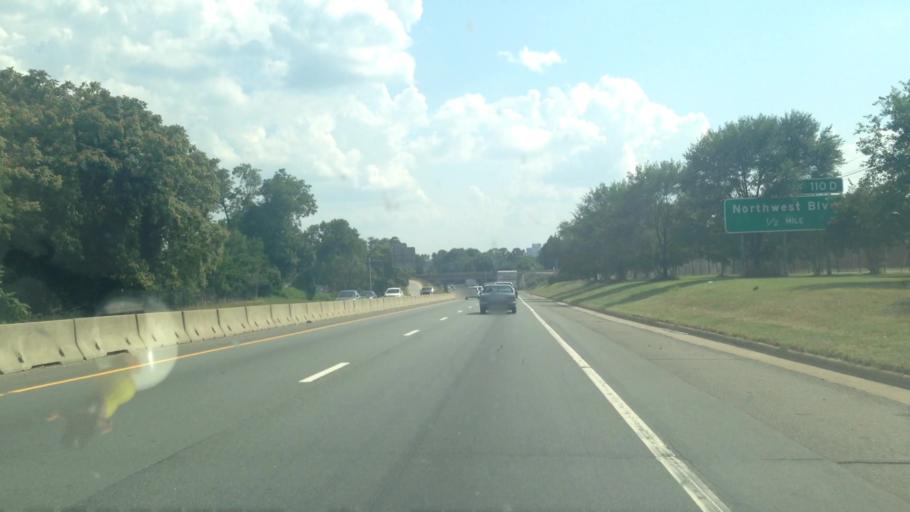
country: US
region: North Carolina
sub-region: Forsyth County
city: Winston-Salem
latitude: 36.1208
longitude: -80.2330
